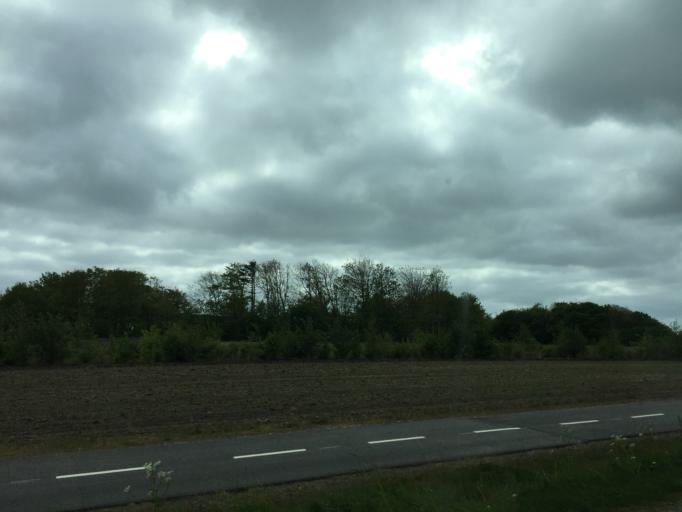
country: DK
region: Central Jutland
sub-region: Ringkobing-Skjern Kommune
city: Ringkobing
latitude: 55.9841
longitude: 8.3431
